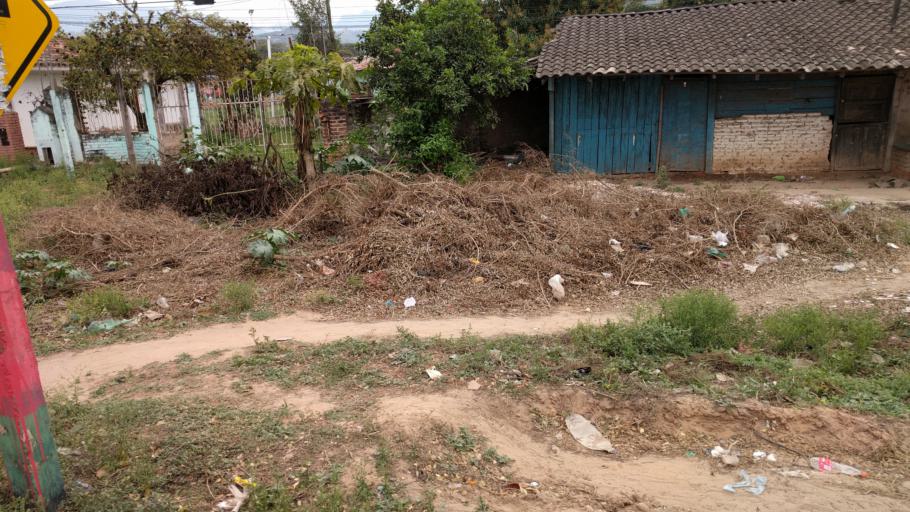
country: BO
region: Santa Cruz
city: Jorochito
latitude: -18.1418
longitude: -63.4797
